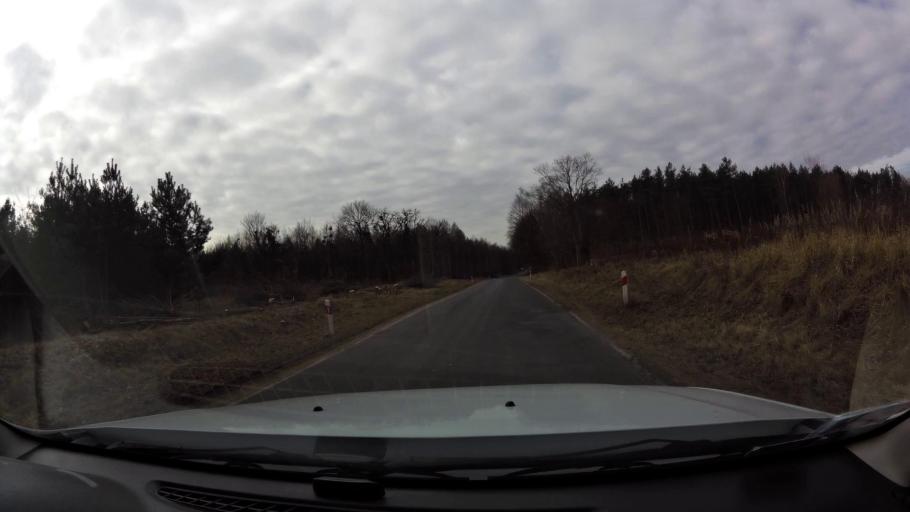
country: PL
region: West Pomeranian Voivodeship
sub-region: Powiat mysliborski
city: Debno
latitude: 52.7178
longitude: 14.6785
